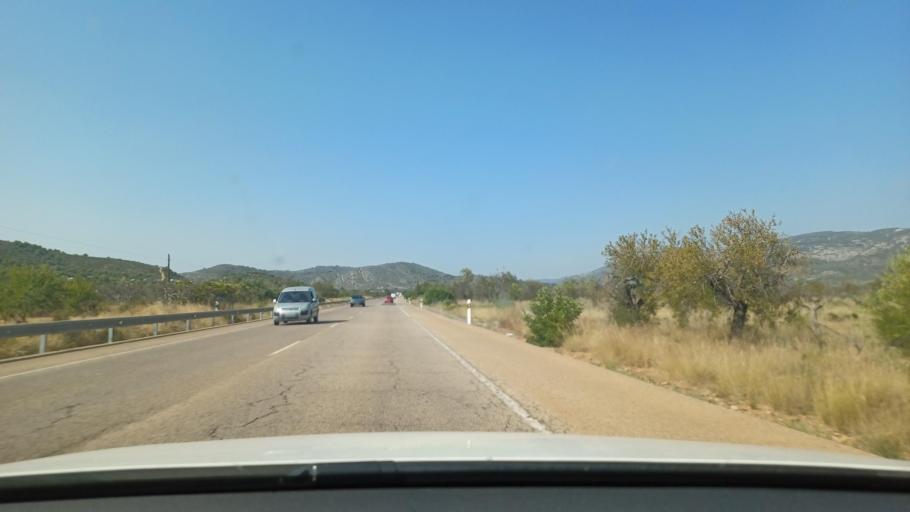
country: ES
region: Valencia
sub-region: Provincia de Castello
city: Alcala de Xivert
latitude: 40.2545
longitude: 0.2358
